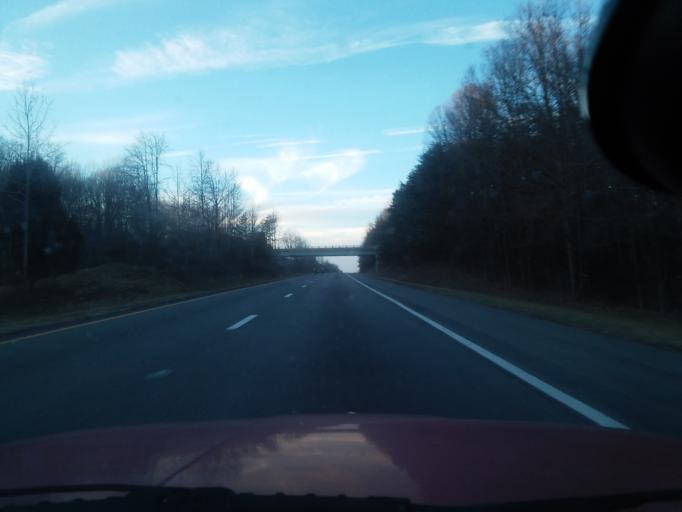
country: US
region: Virginia
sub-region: Louisa County
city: Louisa
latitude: 37.8429
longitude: -77.9803
